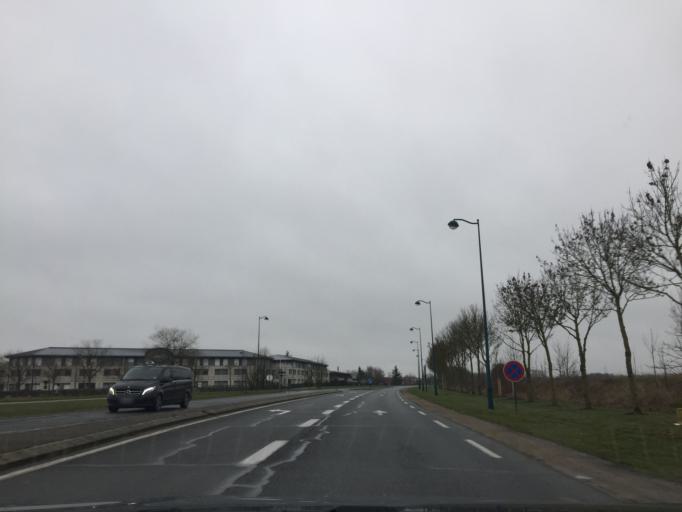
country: FR
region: Ile-de-France
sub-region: Departement de Seine-et-Marne
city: Magny-le-Hongre
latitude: 48.8680
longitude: 2.8072
